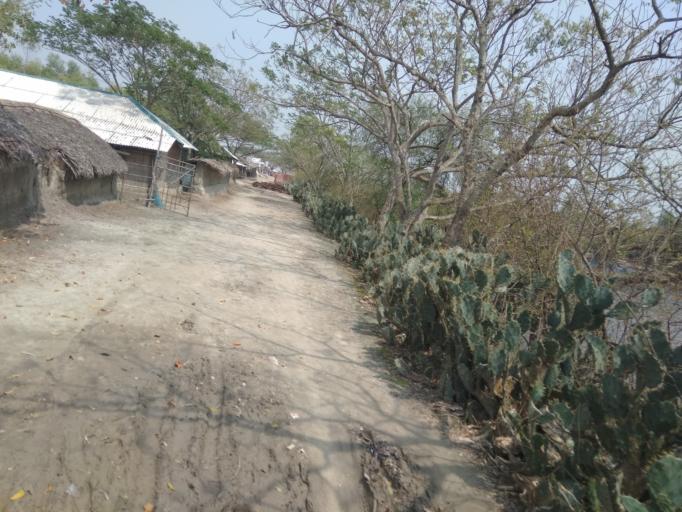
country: IN
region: West Bengal
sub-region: North 24 Parganas
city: Taki
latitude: 22.2873
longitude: 89.2731
